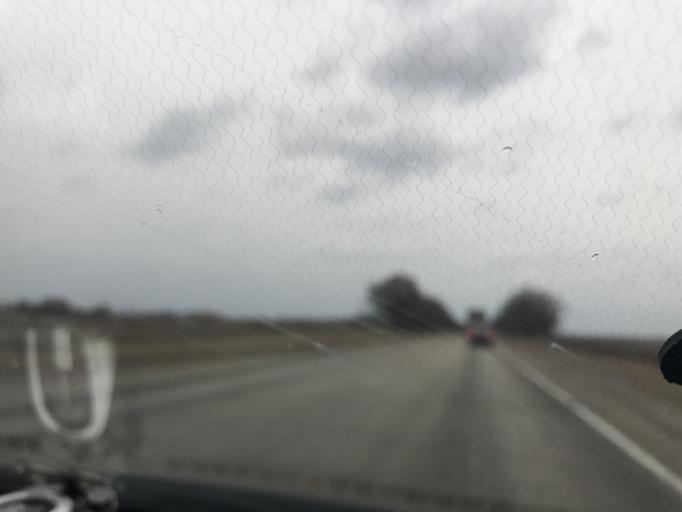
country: RU
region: Krasnodarskiy
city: Novoleushkovskaya
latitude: 46.0030
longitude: 40.0190
